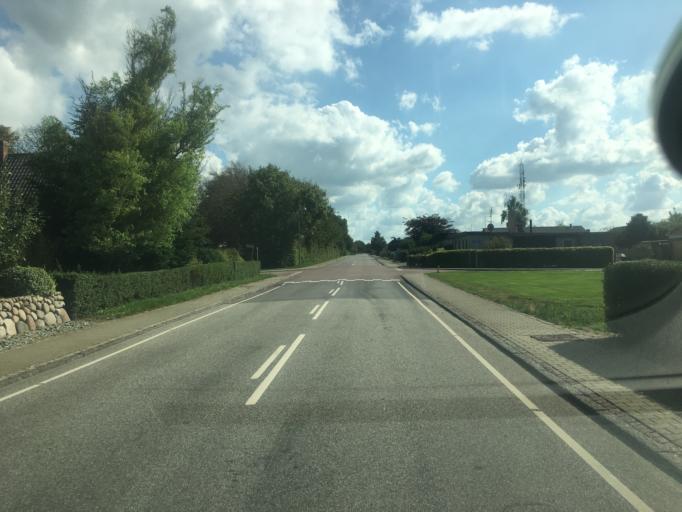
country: DE
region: Schleswig-Holstein
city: Ellhoft
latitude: 54.9395
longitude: 8.9687
